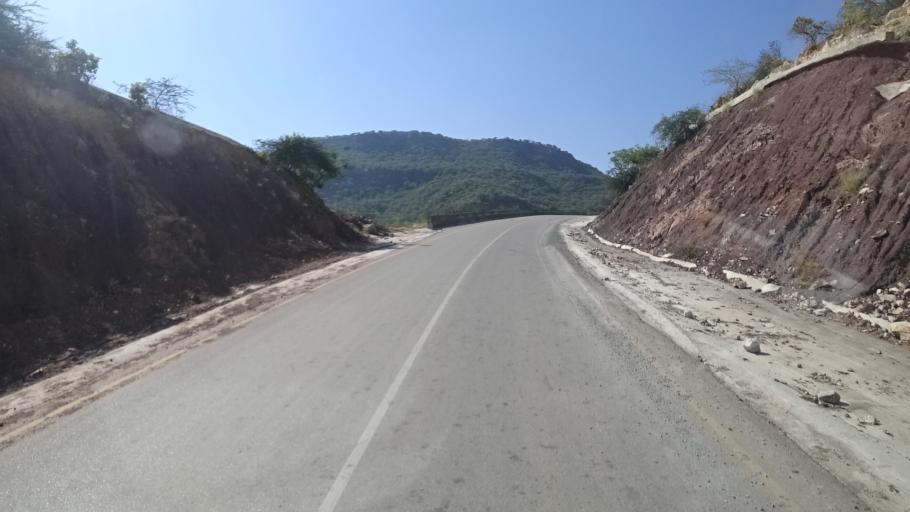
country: OM
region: Zufar
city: Salalah
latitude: 17.0534
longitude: 54.6116
